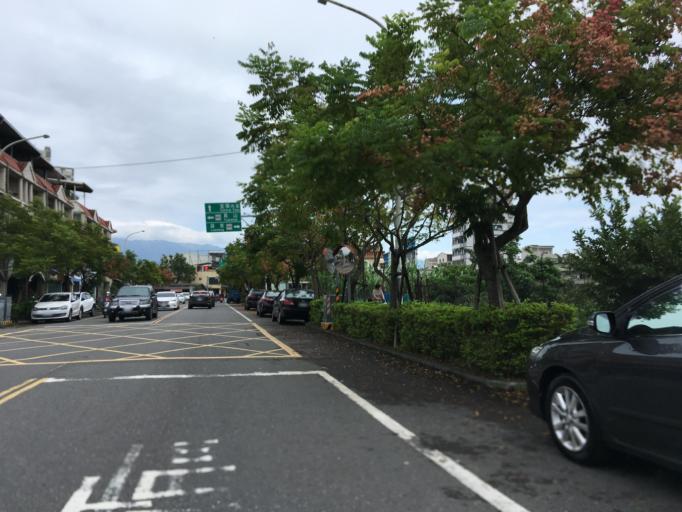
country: TW
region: Taiwan
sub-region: Yilan
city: Yilan
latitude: 24.7414
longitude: 121.7534
